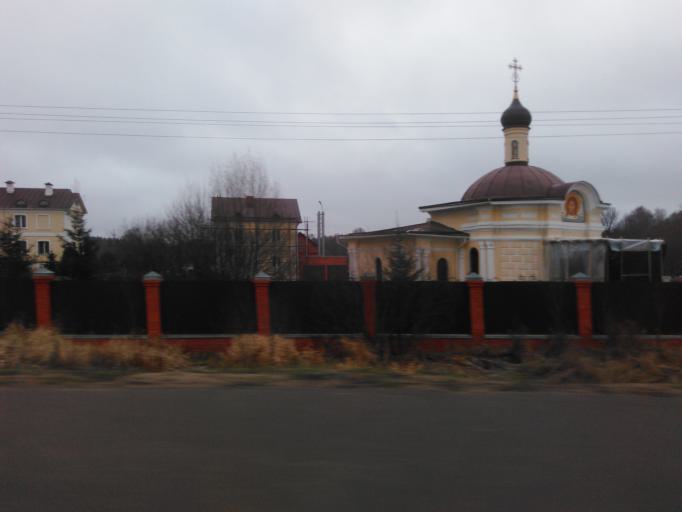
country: RU
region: Moskovskaya
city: Ashukino
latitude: 56.1273
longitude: 37.9740
